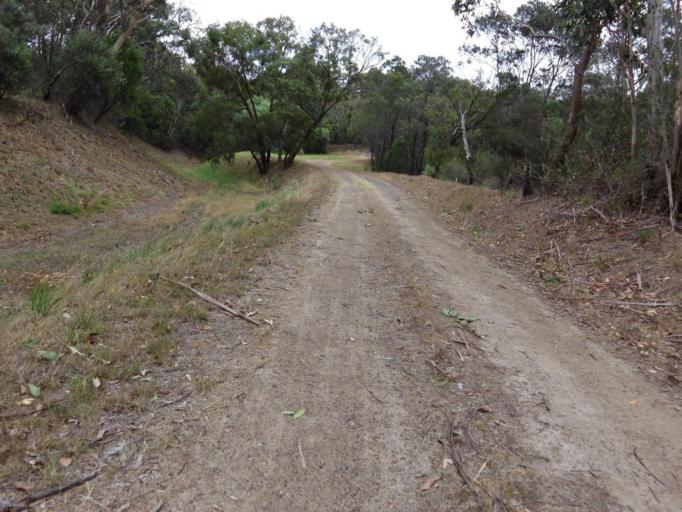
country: AU
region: Victoria
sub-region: Frankston
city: Frankston South
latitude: -38.1827
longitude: 145.1304
